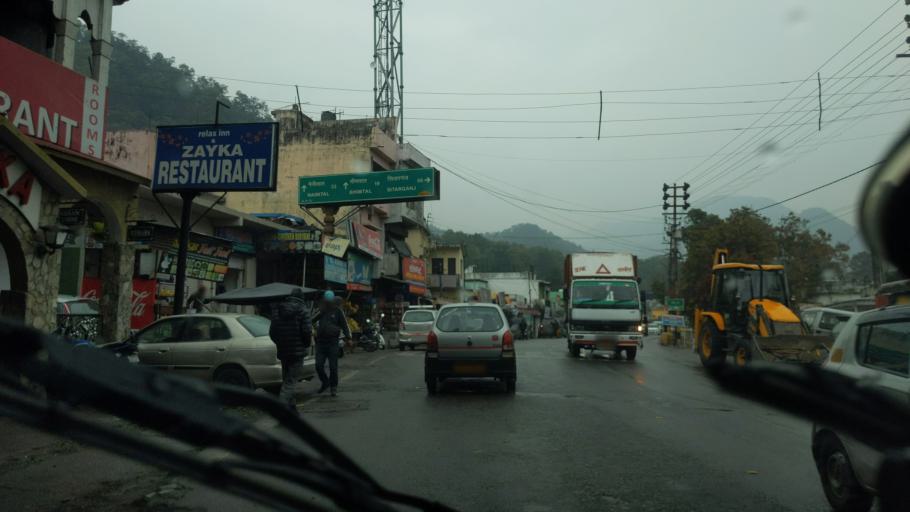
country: IN
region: Uttarakhand
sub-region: Naini Tal
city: Haldwani
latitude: 29.2695
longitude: 79.5441
